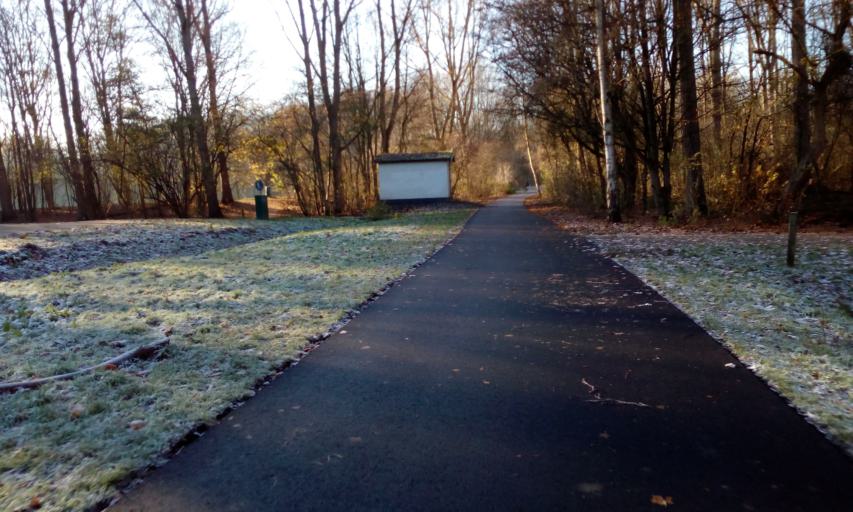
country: NL
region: South Holland
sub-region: Gemeente Lansingerland
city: Bergschenhoek
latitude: 51.9713
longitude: 4.5193
